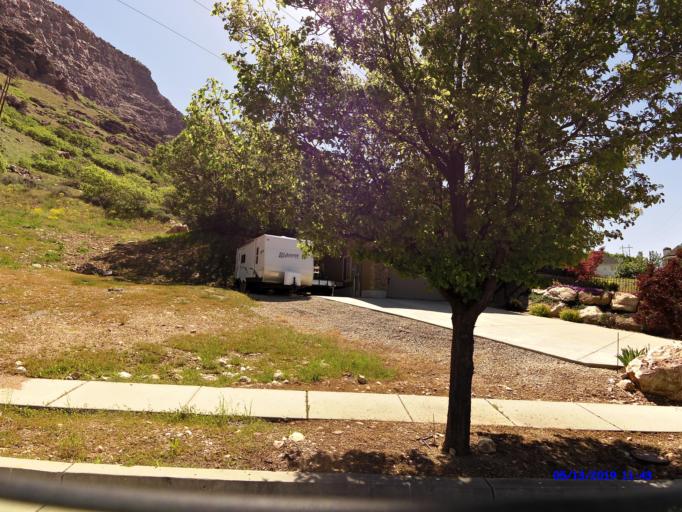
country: US
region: Utah
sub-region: Weber County
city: North Ogden
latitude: 41.2744
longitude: -111.9482
